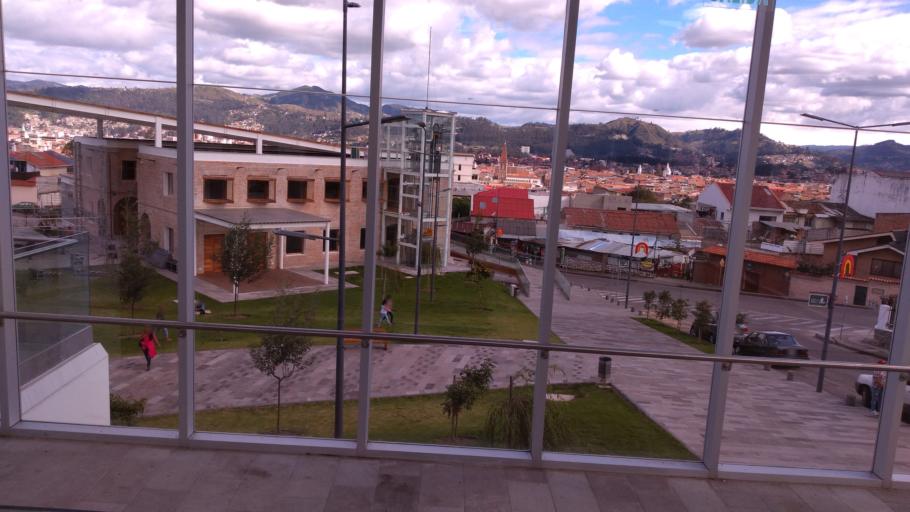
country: EC
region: Azuay
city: Cuenca
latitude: -2.8866
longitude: -79.0078
